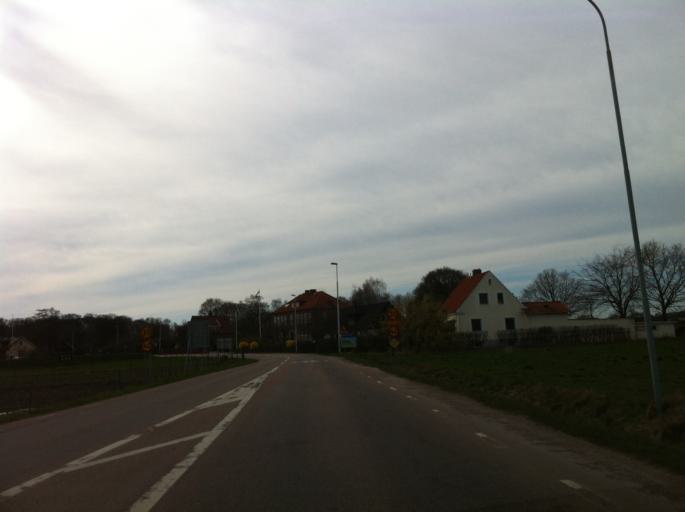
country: SE
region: Skane
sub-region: Hoganas Kommun
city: Hoganas
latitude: 56.2619
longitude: 12.5810
